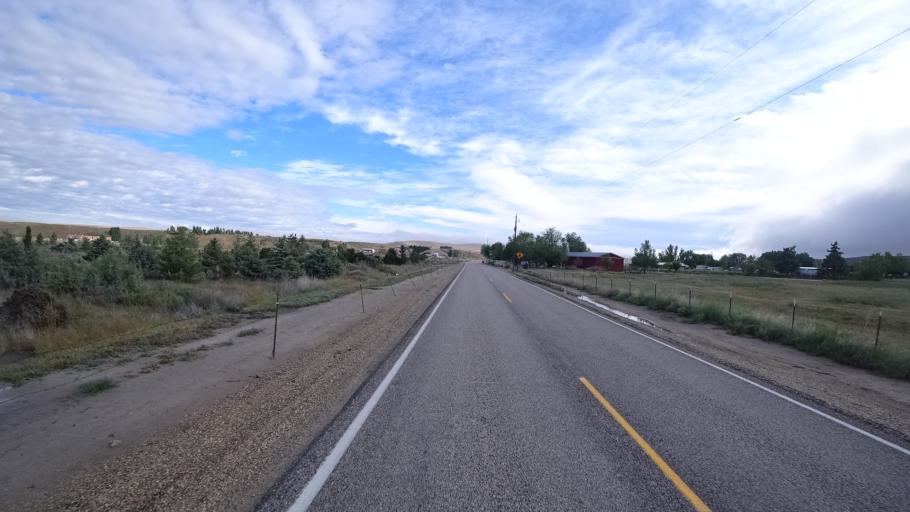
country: US
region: Idaho
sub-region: Ada County
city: Star
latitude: 43.7773
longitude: -116.4730
